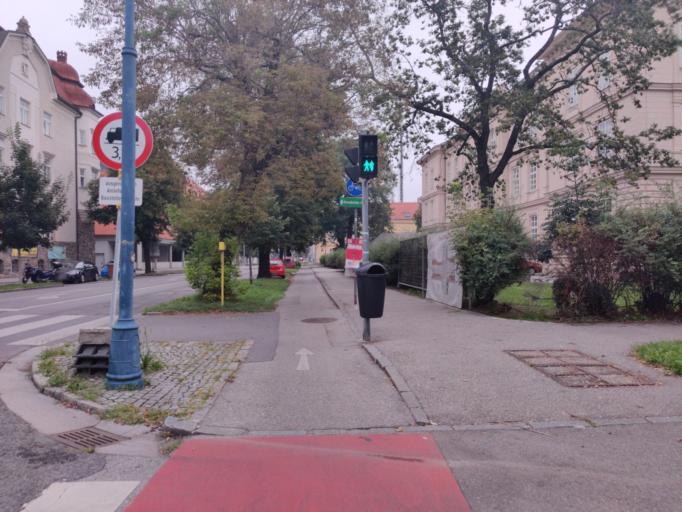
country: AT
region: Lower Austria
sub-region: Politischer Bezirk Krems
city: Weinzierl bei Krems
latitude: 48.4084
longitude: 15.5993
